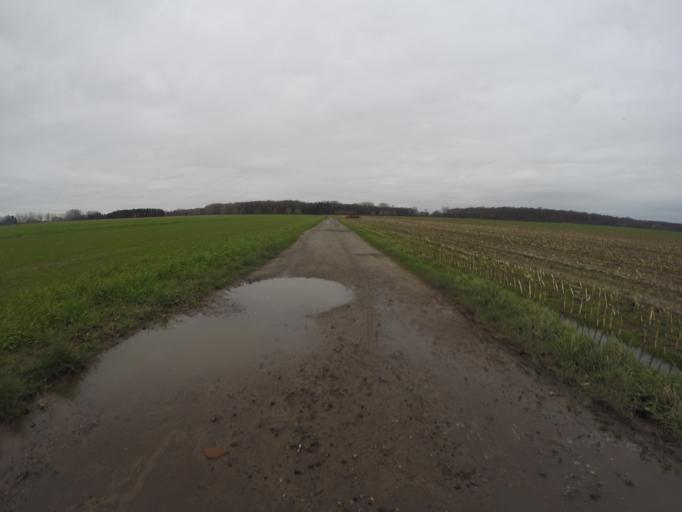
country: BE
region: Flanders
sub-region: Provincie Oost-Vlaanderen
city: Aalter
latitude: 51.1231
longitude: 3.4523
